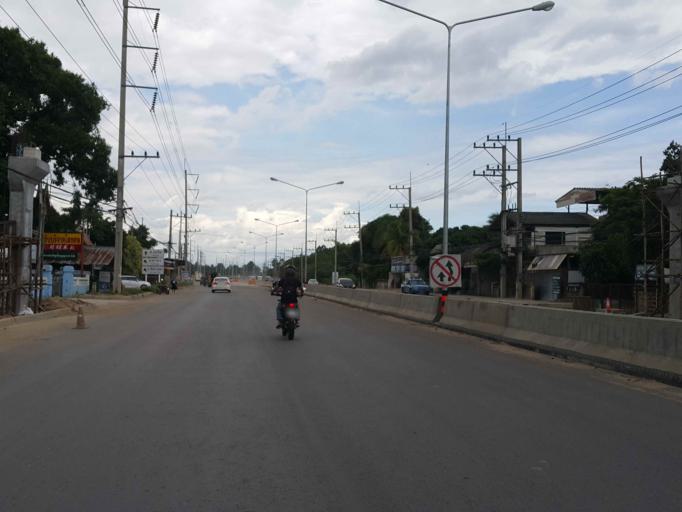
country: TH
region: Chiang Mai
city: Chiang Mai
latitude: 18.8614
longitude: 98.9659
